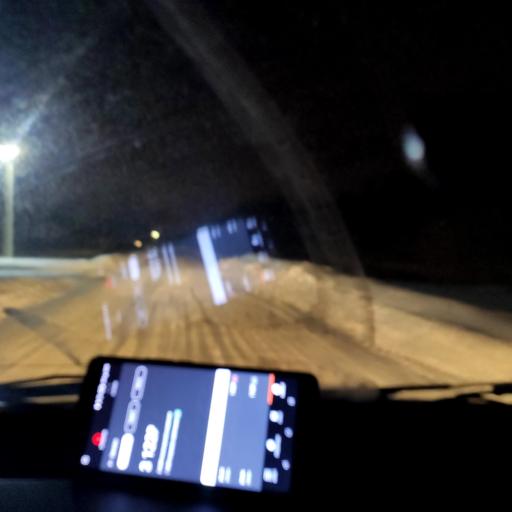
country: RU
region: Bashkortostan
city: Ufa
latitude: 54.6796
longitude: 56.0190
